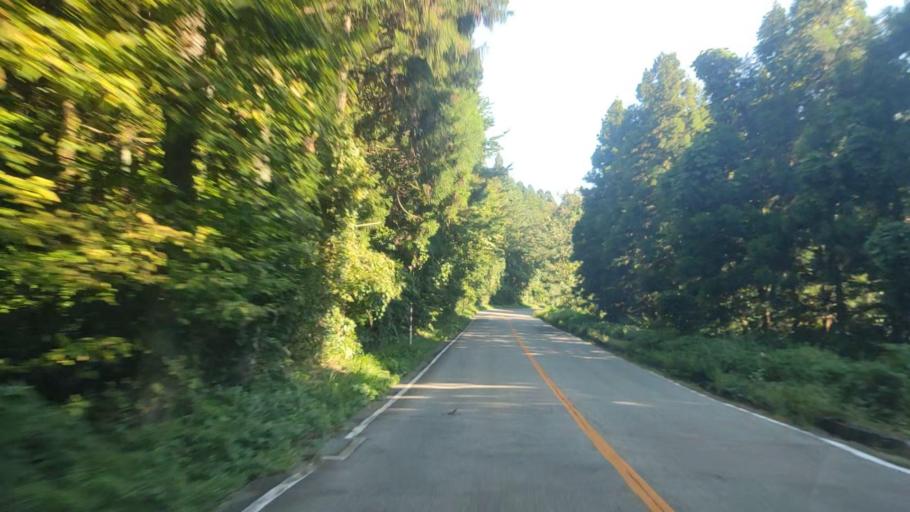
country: JP
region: Ishikawa
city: Nanao
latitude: 37.1067
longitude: 136.9466
